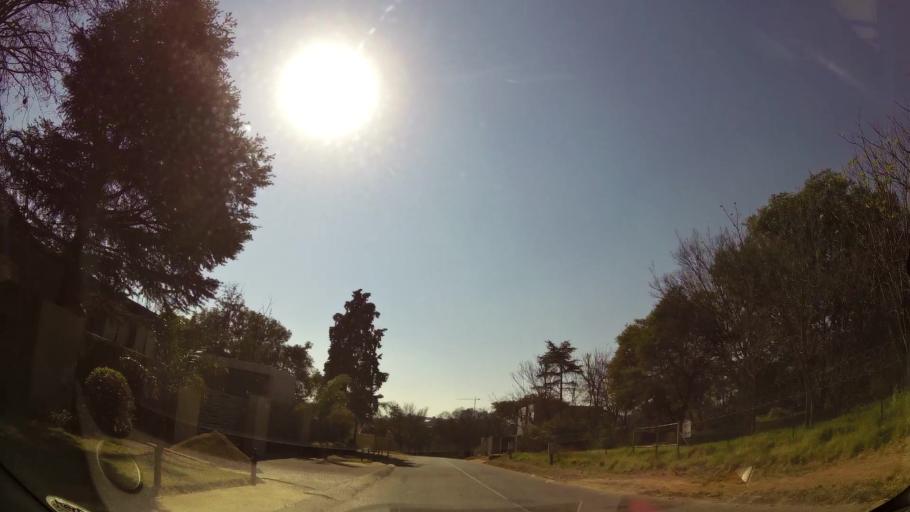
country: ZA
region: Gauteng
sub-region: City of Johannesburg Metropolitan Municipality
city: Johannesburg
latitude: -26.1069
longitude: 28.0438
